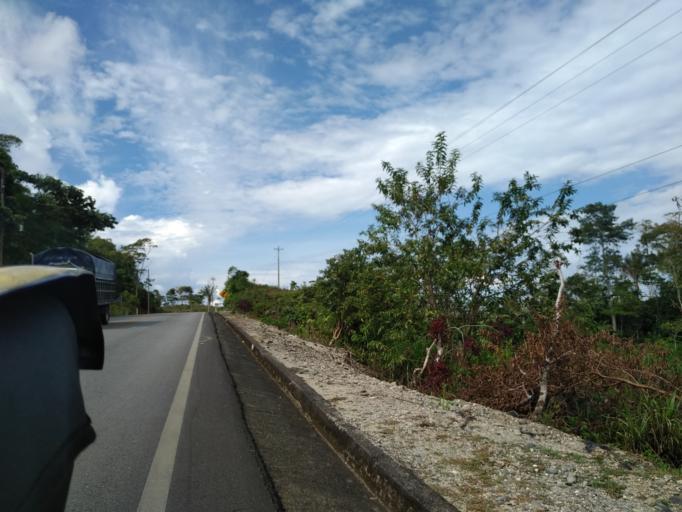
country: EC
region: Napo
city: Tena
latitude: -1.1059
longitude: -77.8044
